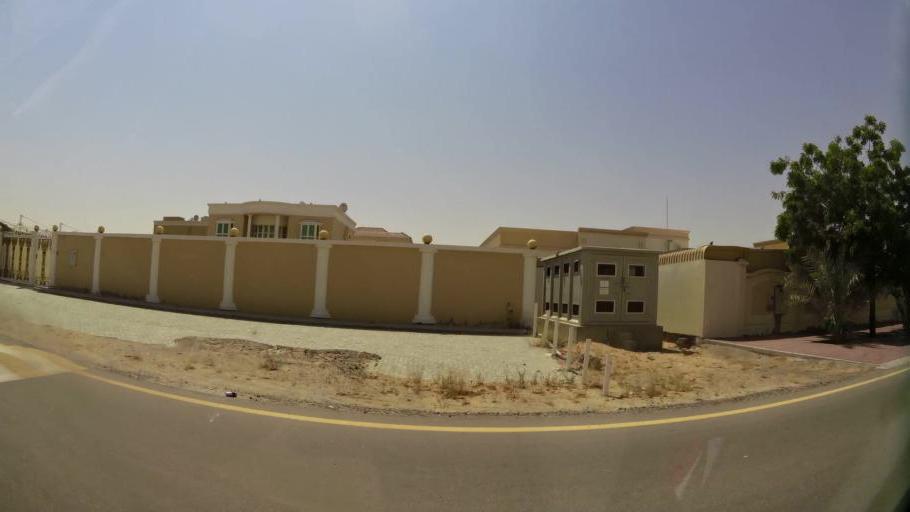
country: AE
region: Ajman
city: Ajman
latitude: 25.4227
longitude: 55.5235
